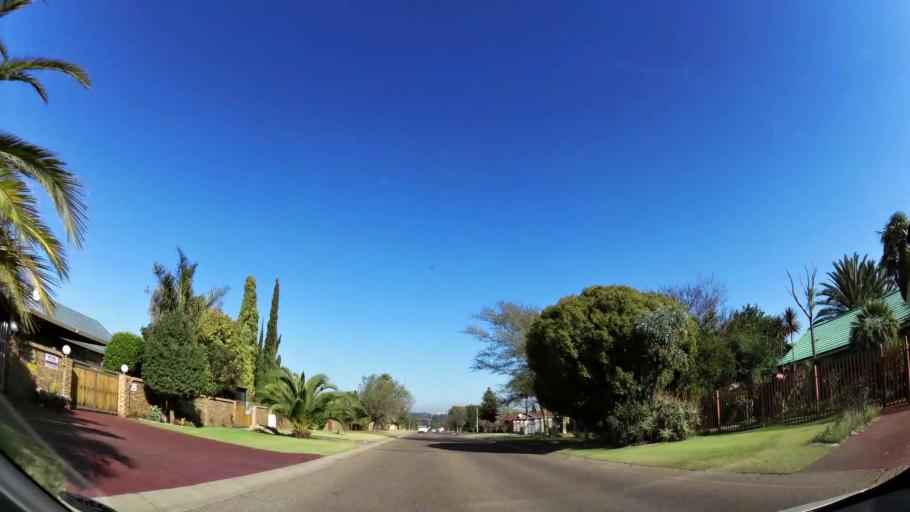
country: ZA
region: Mpumalanga
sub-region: Nkangala District Municipality
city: Witbank
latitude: -25.8864
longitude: 29.2520
